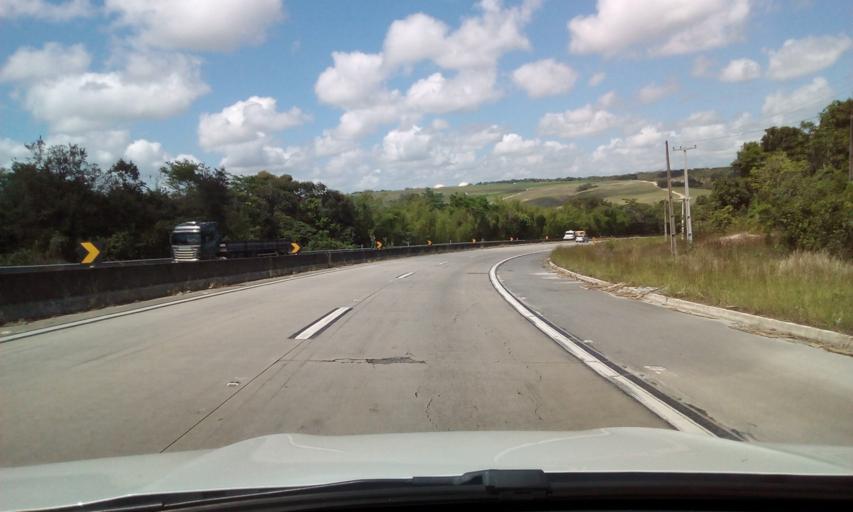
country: BR
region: Paraiba
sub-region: Alhandra
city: Alhandra
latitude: -7.4379
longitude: -34.9769
